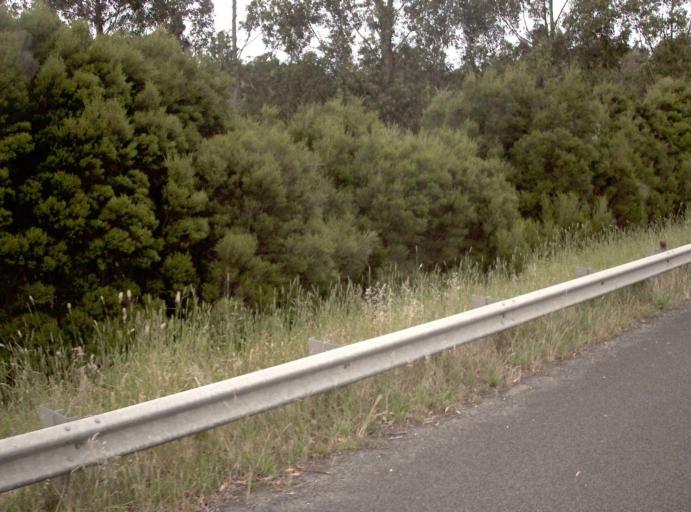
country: AU
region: Victoria
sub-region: Cardinia
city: Koo-Wee-Rup
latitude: -38.3634
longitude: 145.6606
